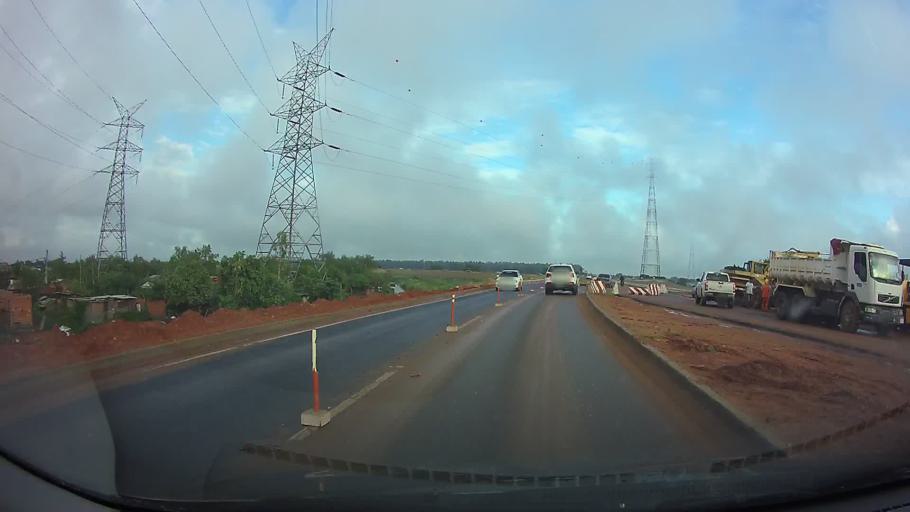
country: PY
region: Asuncion
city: Asuncion
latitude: -25.2471
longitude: -57.5874
